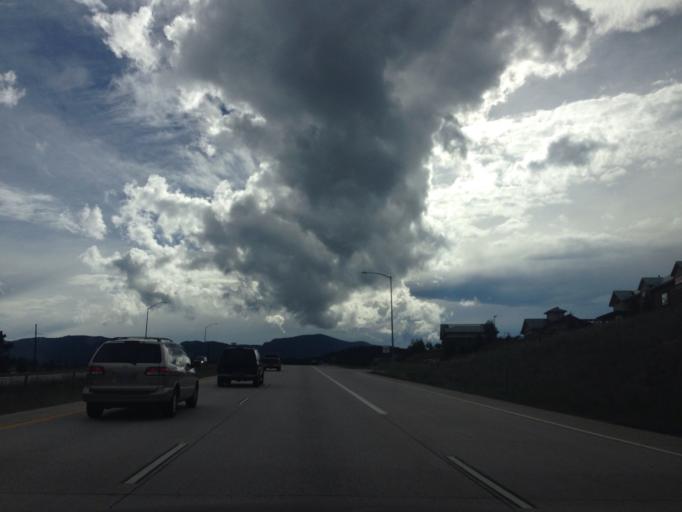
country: US
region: Colorado
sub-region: Jefferson County
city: Indian Hills
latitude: 39.5431
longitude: -105.2882
